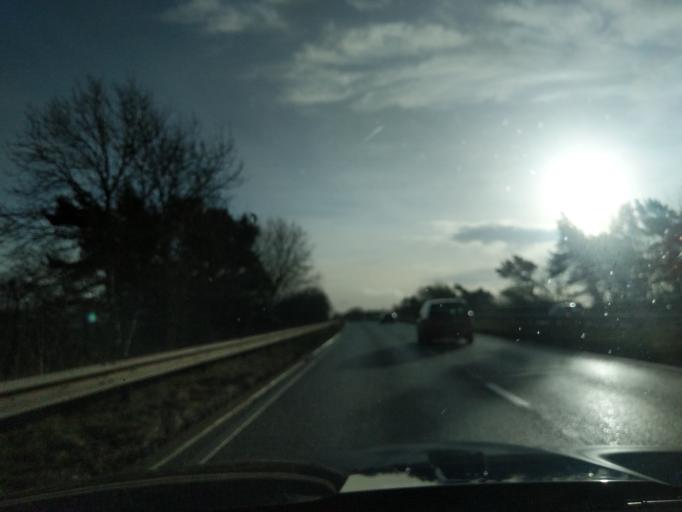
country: GB
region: England
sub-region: Northumberland
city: Seghill
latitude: 55.0466
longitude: -1.5520
